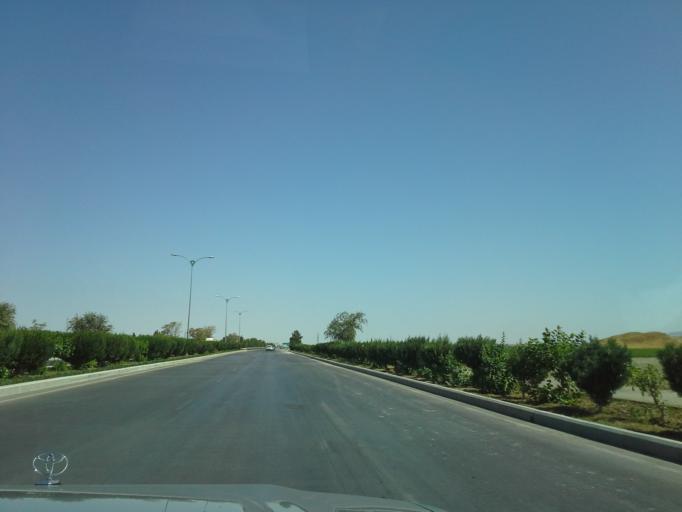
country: TM
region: Ahal
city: Annau
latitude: 37.9062
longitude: 58.5273
